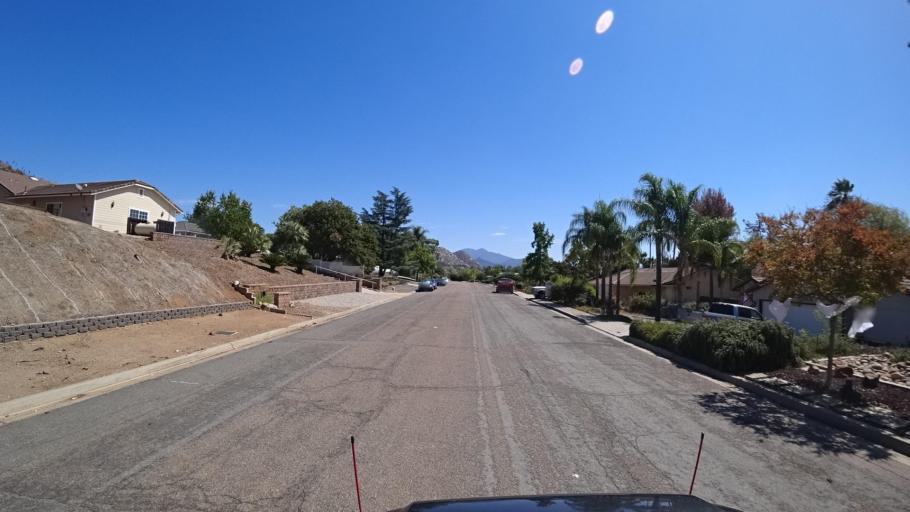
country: US
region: California
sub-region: San Diego County
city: San Diego Country Estates
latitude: 33.0210
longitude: -116.8145
